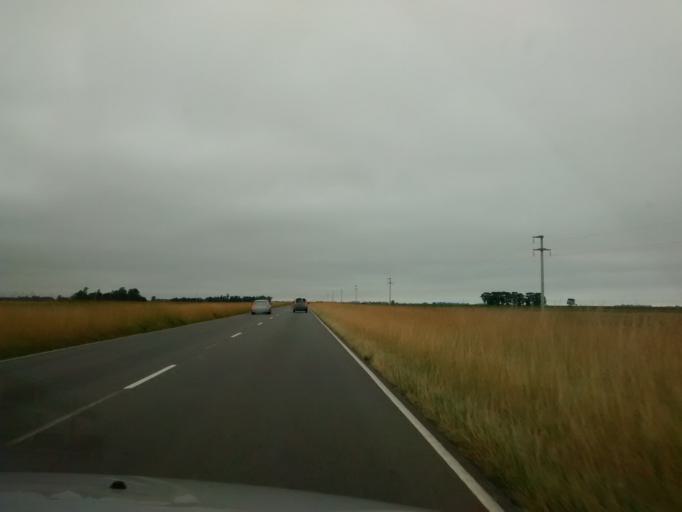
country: AR
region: Buenos Aires
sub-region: Partido de Ayacucho
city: Ayacucho
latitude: -37.0368
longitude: -58.5405
